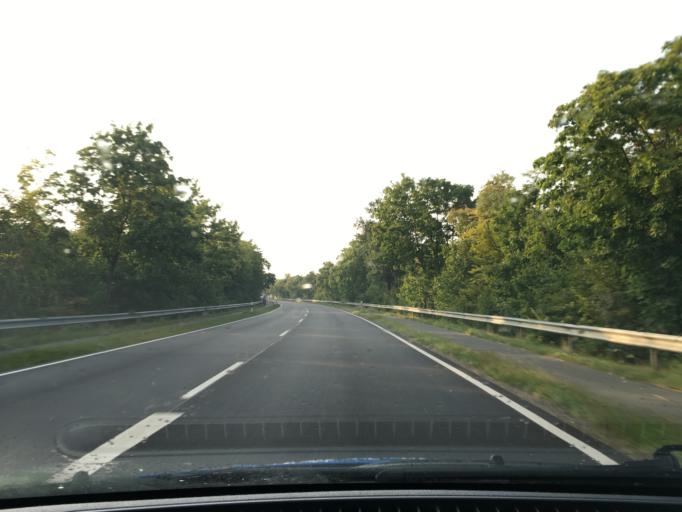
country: DE
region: Lower Saxony
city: Celle
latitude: 52.6414
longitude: 10.0774
